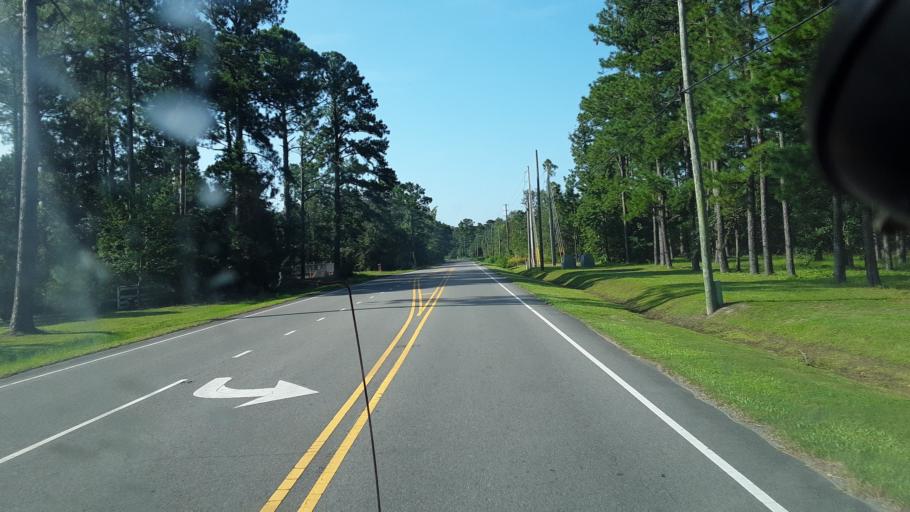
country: US
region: North Carolina
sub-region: Brunswick County
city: Belville
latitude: 34.1828
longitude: -77.9895
